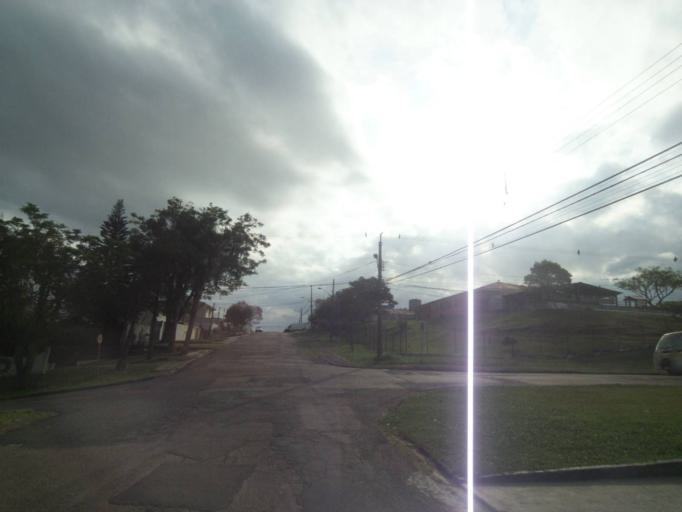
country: BR
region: Parana
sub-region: Pinhais
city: Pinhais
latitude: -25.4047
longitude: -49.1982
